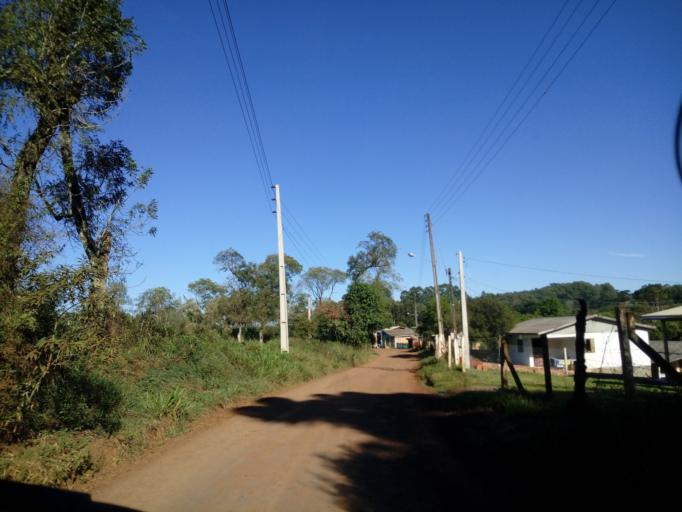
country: BR
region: Santa Catarina
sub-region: Chapeco
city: Chapeco
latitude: -27.2038
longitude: -52.6778
